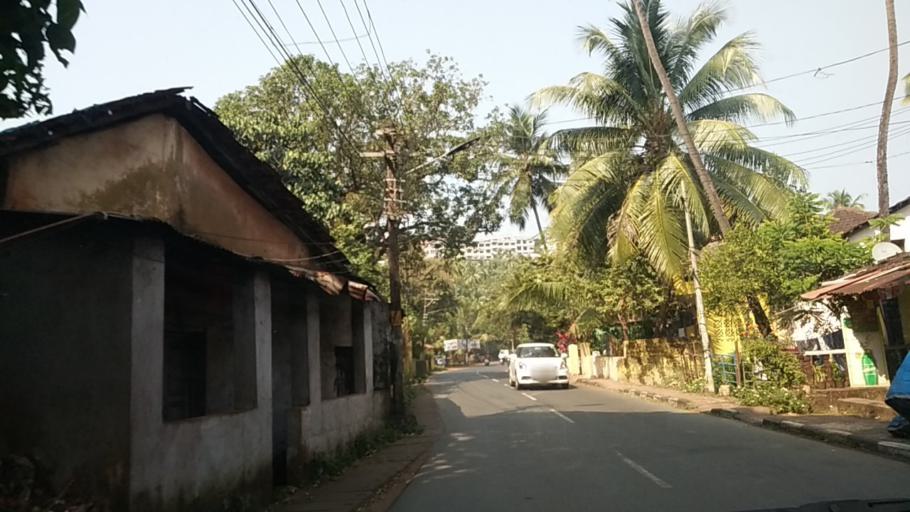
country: IN
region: Goa
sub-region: North Goa
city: Bambolim
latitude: 15.5026
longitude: 73.8696
